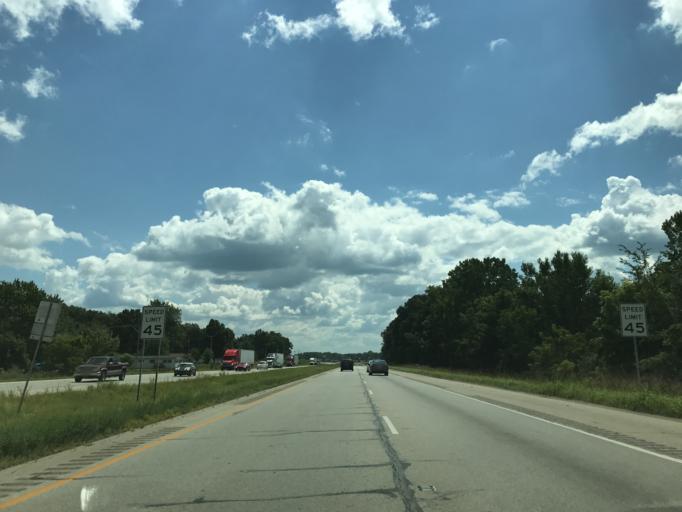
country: US
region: Indiana
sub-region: Kosciusko County
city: Winona Lake
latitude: 41.2460
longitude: -85.8226
